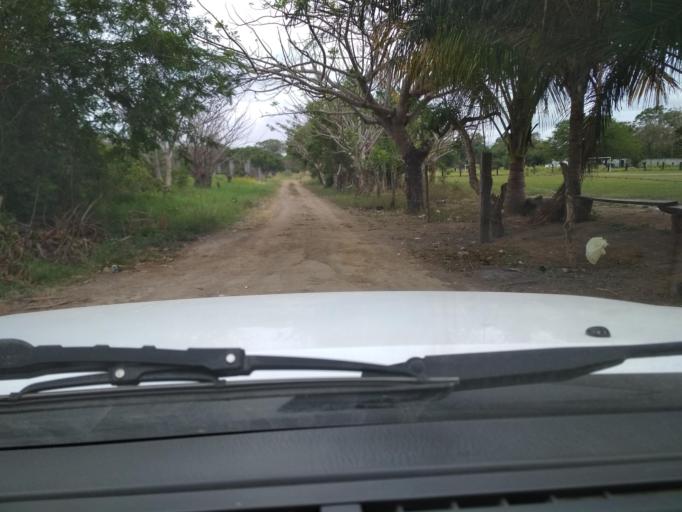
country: MX
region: Veracruz
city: Paso del Toro
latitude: 19.0547
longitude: -96.1374
